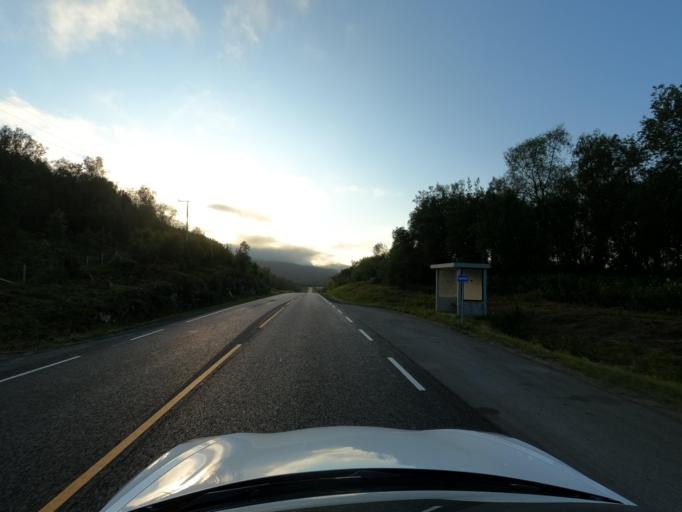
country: NO
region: Troms
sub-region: Skanland
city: Evenskjer
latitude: 68.6752
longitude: 16.5651
